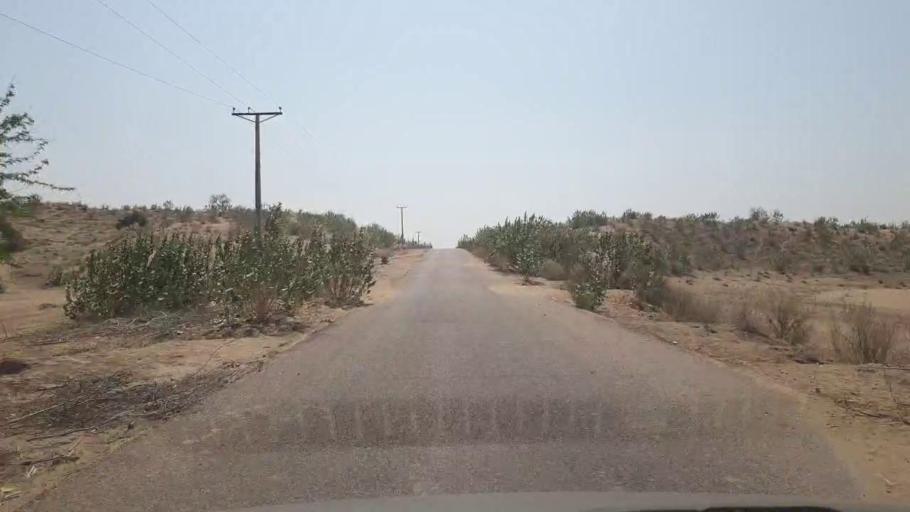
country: PK
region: Sindh
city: Chor
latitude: 25.6214
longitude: 70.1756
